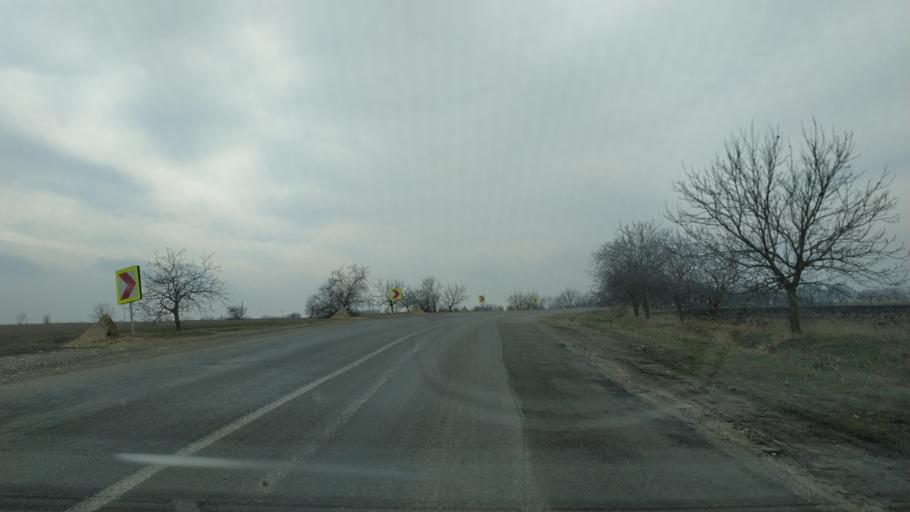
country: MD
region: Cahul
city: Cahul
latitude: 45.9348
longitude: 28.3440
